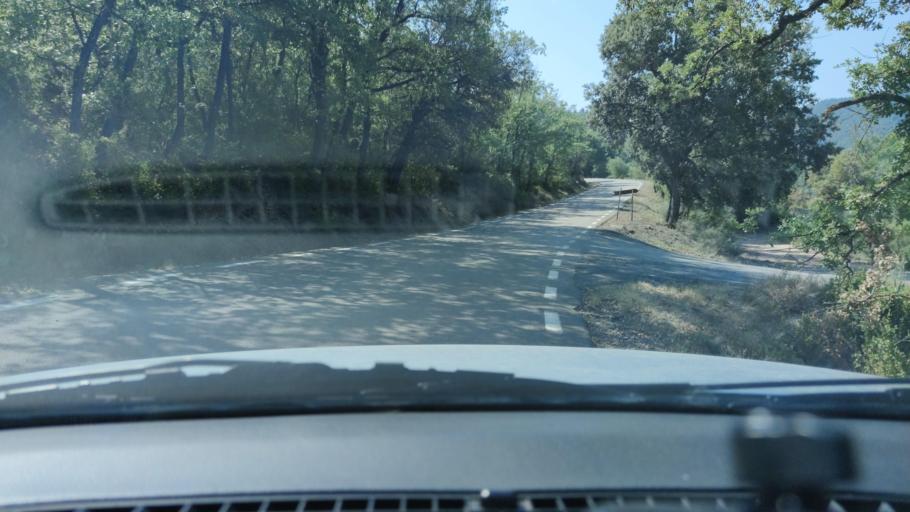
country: ES
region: Catalonia
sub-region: Provincia de Lleida
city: Senterada
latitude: 42.2694
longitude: 0.9526
